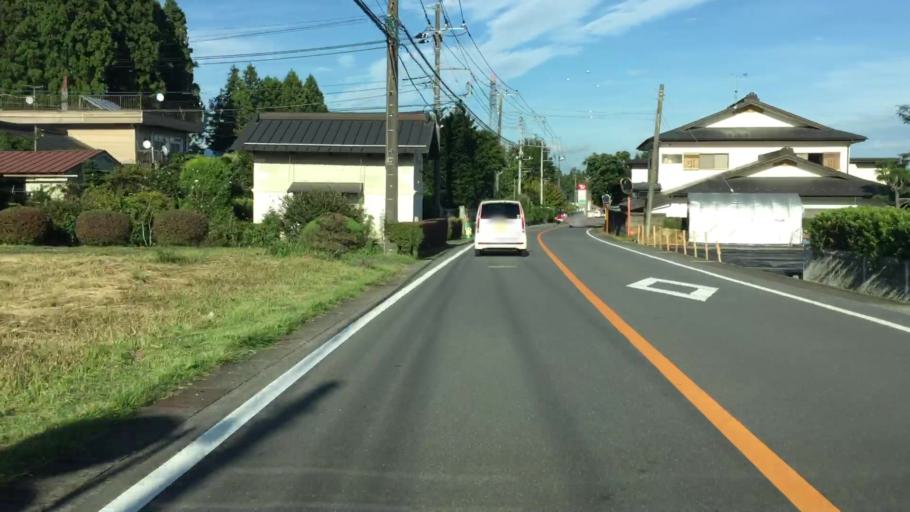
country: JP
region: Tochigi
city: Imaichi
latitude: 36.7374
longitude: 139.7050
